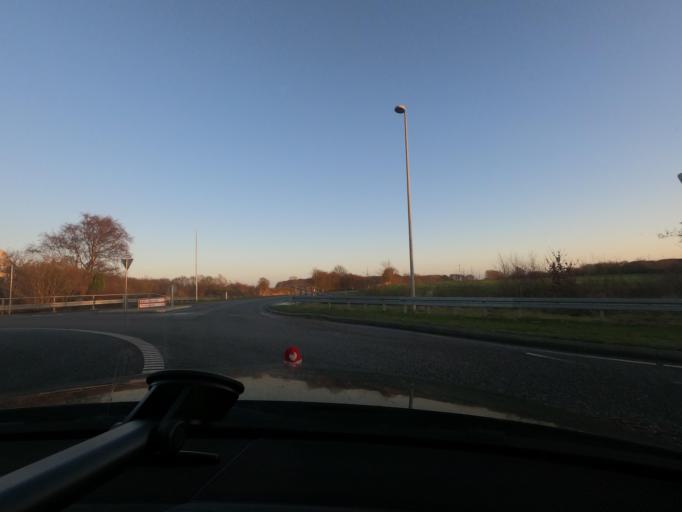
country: DK
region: South Denmark
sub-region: Sonderborg Kommune
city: Horuphav
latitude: 54.9205
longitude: 9.8977
